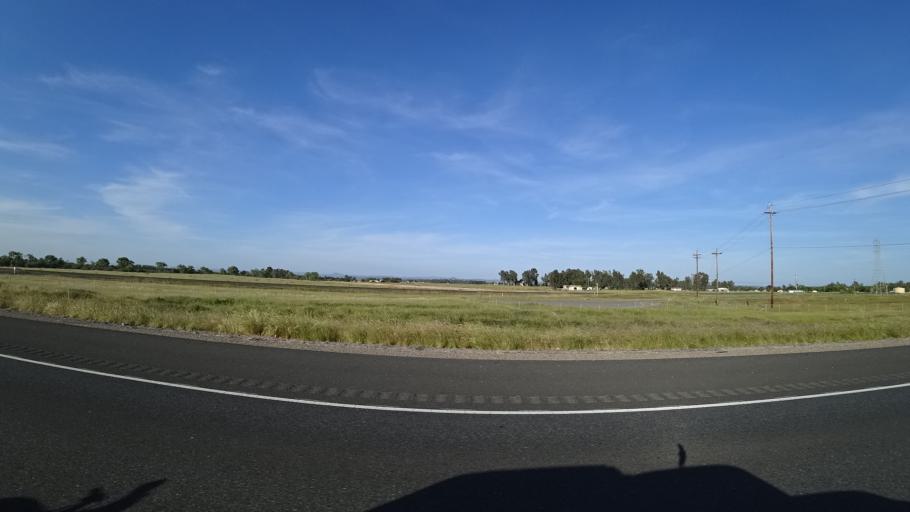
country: US
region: California
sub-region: Placer County
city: Sheridan
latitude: 38.9877
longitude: -121.3867
